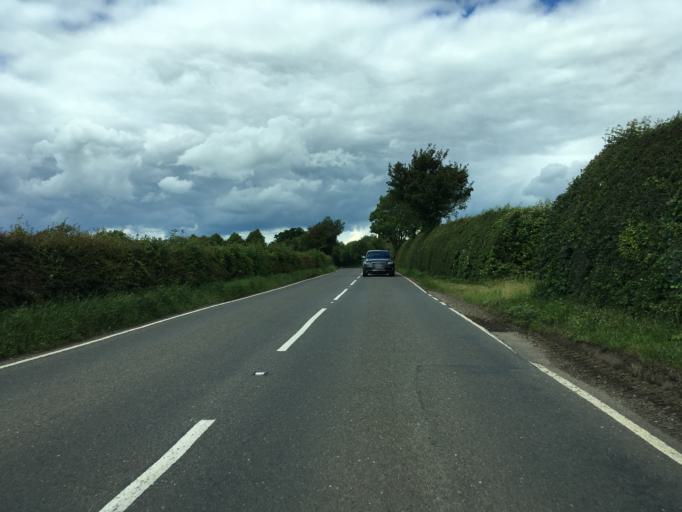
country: GB
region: England
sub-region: Northamptonshire
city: Brackley
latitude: 52.0757
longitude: -1.1240
